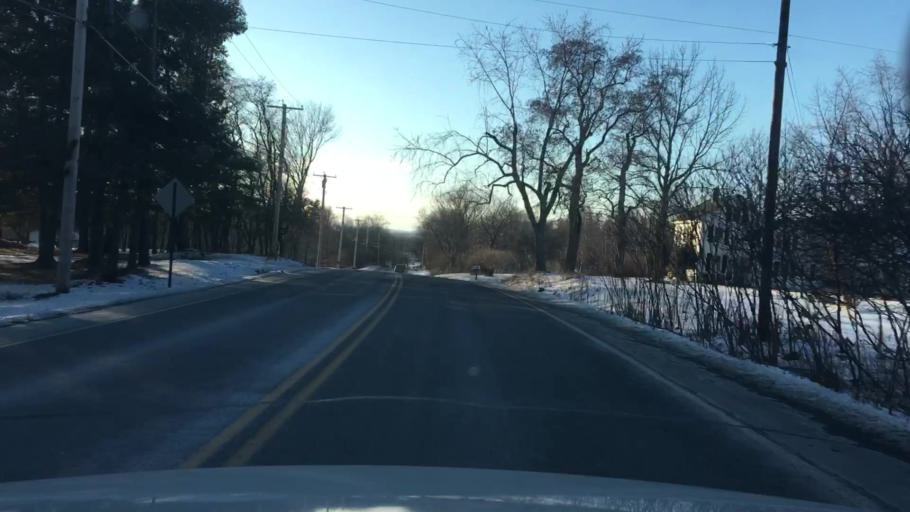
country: US
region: Maine
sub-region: Penobscot County
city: Eddington
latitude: 44.8302
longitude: -68.6661
